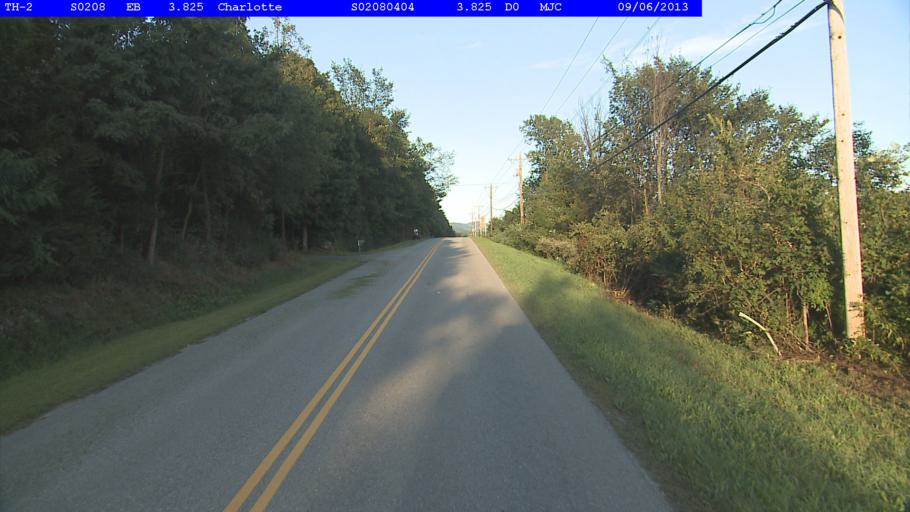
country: US
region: Vermont
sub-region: Chittenden County
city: Hinesburg
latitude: 44.3218
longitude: -73.1720
